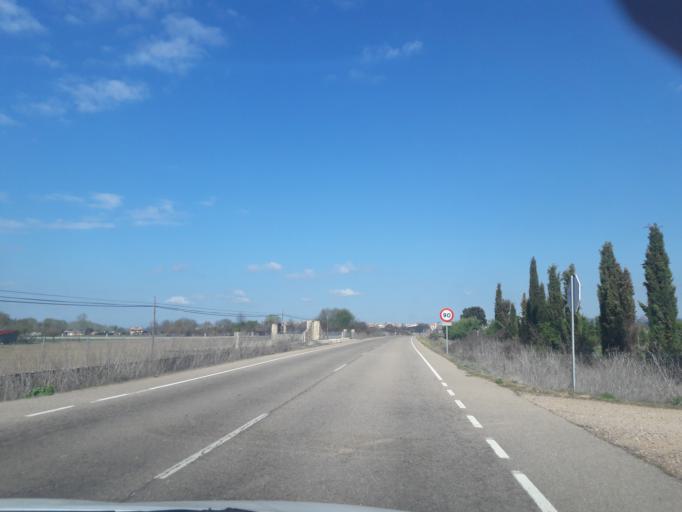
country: ES
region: Castille and Leon
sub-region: Provincia de Salamanca
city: Ciudad Rodrigo
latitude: 40.5803
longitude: -6.5045
